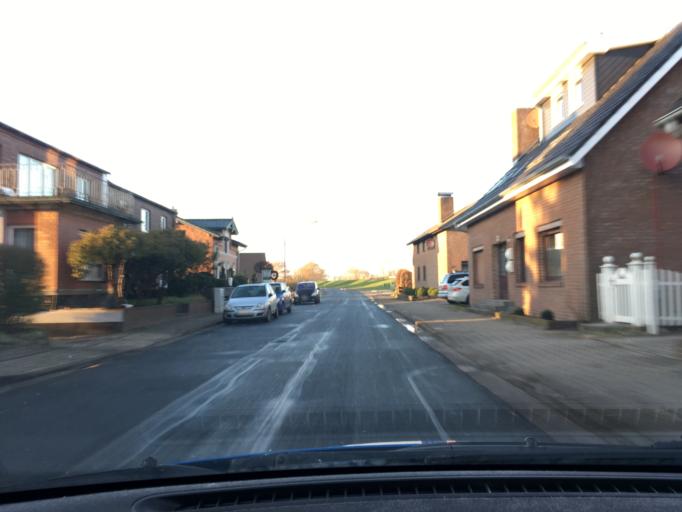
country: DE
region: Lower Saxony
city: Stelle
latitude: 53.4534
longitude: 10.0678
